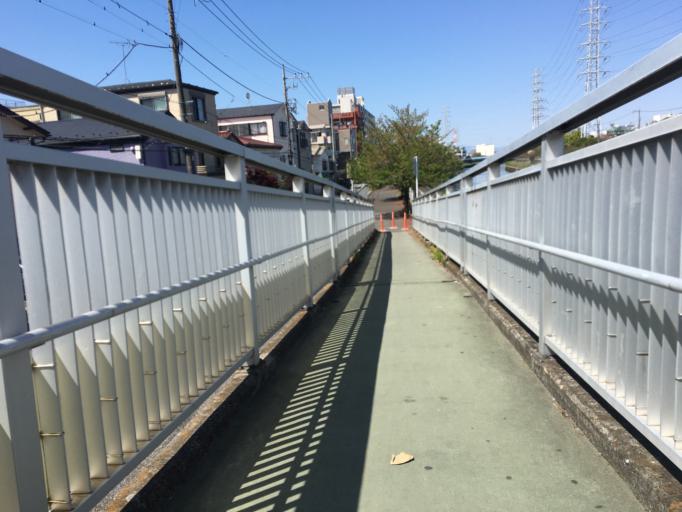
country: JP
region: Saitama
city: Shimotoda
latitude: 35.7928
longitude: 139.6593
